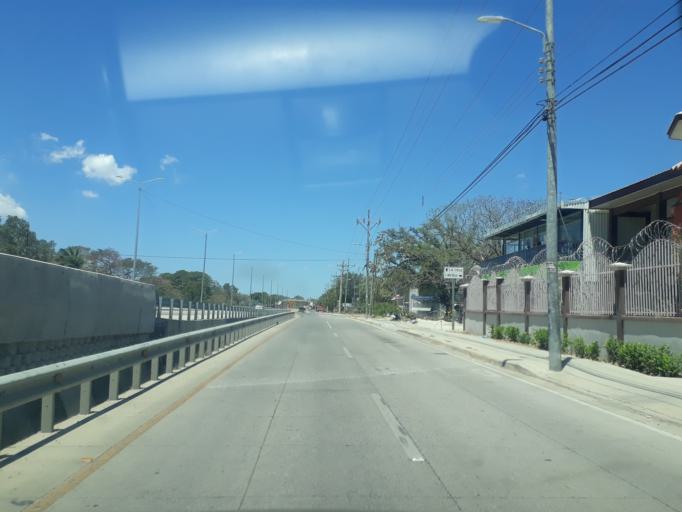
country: CR
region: Guanacaste
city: Liberia
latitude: 10.6332
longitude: -85.4478
